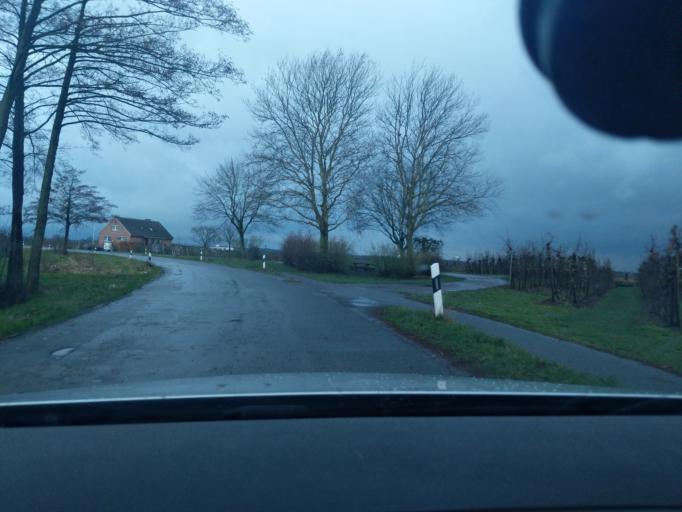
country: DE
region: Lower Saxony
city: Mittelnkirchen
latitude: 53.5312
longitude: 9.6469
